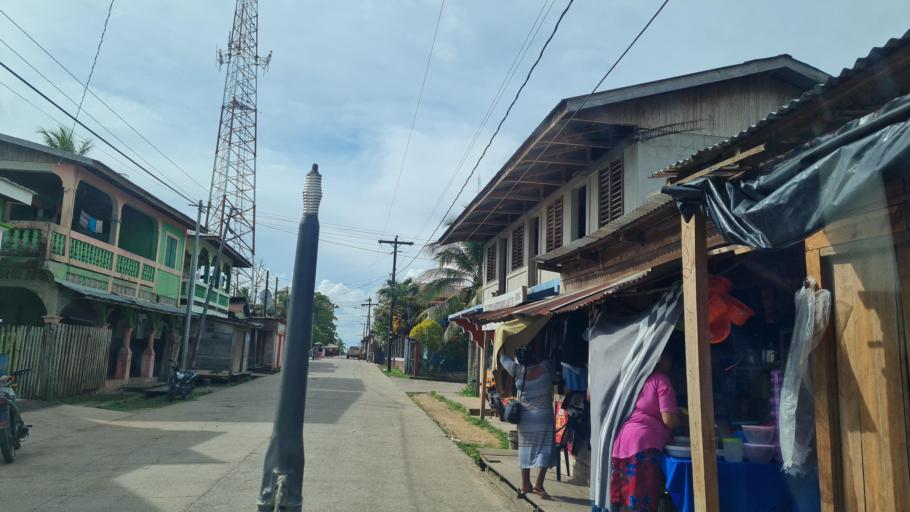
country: NI
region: Atlantico Norte (RAAN)
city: Waspam
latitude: 14.7409
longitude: -83.9710
